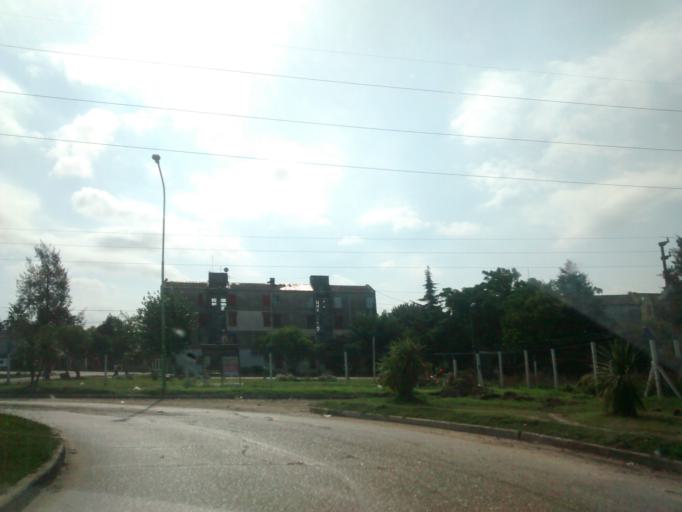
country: AR
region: Buenos Aires
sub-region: Partido de La Plata
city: La Plata
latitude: -34.9436
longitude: -57.9097
